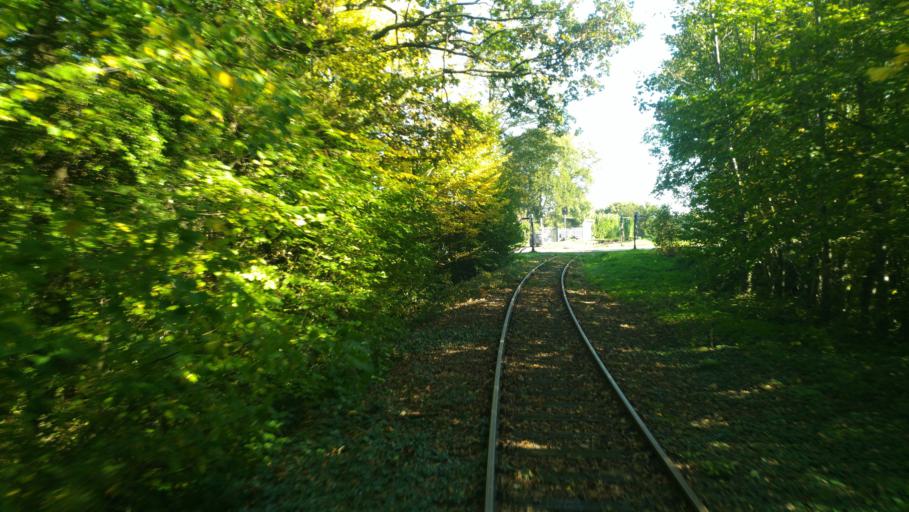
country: DE
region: Lower Saxony
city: Nienstadt
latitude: 52.3000
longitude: 9.1637
